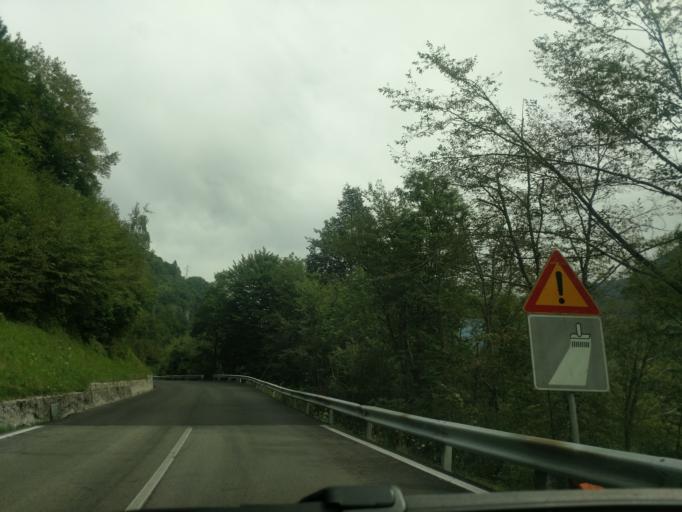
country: IT
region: Veneto
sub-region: Provincia di Belluno
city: Longarone
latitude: 46.2707
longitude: 12.2546
